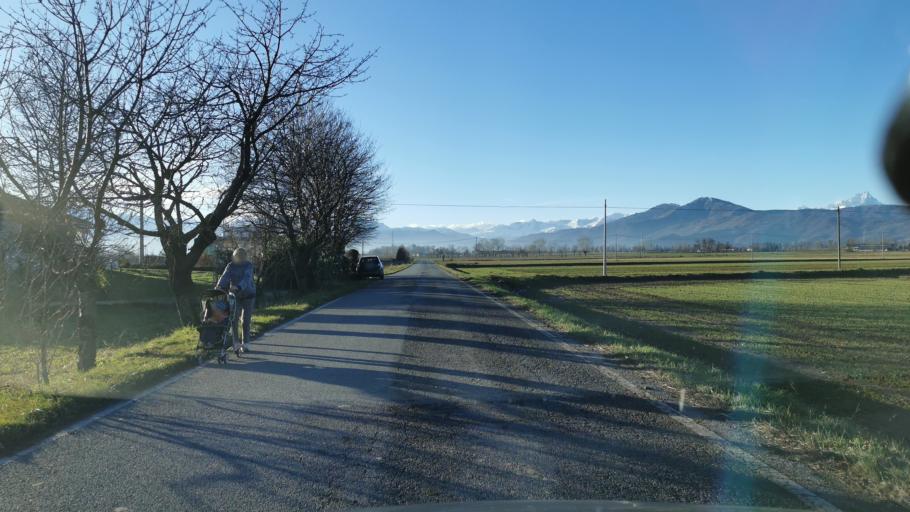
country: IT
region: Piedmont
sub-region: Provincia di Cuneo
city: Roata Rossi
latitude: 44.4579
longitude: 7.5110
